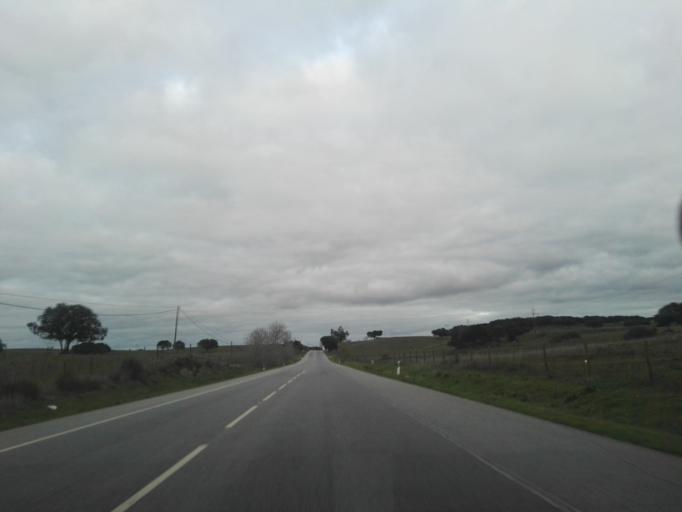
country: PT
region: Evora
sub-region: Montemor-O-Novo
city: Montemor-o-Novo
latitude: 38.6447
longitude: -8.1780
